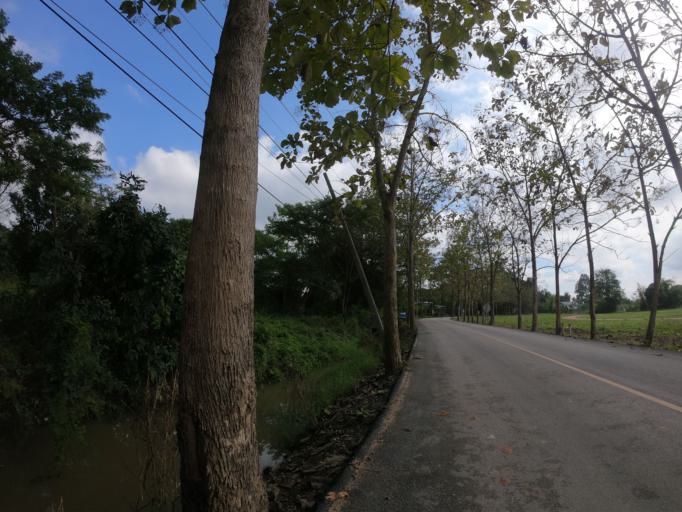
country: TH
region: Chiang Mai
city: San Sai
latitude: 18.8619
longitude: 99.0263
